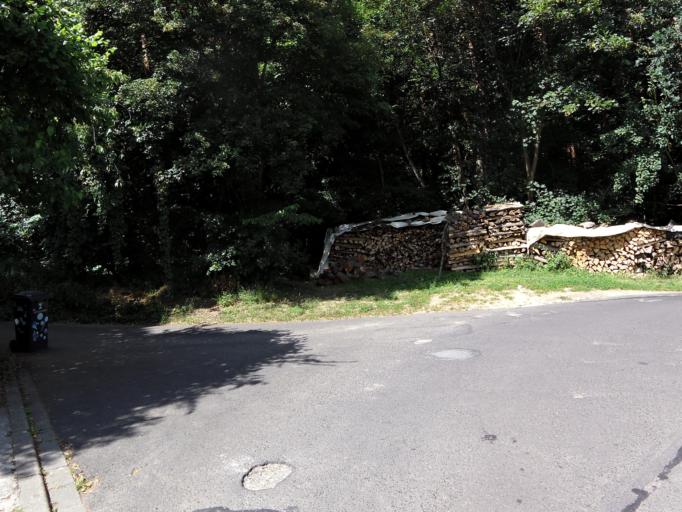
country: DE
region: Bavaria
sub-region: Regierungsbezirk Unterfranken
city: Gadheim
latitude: 49.8324
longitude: 9.9155
